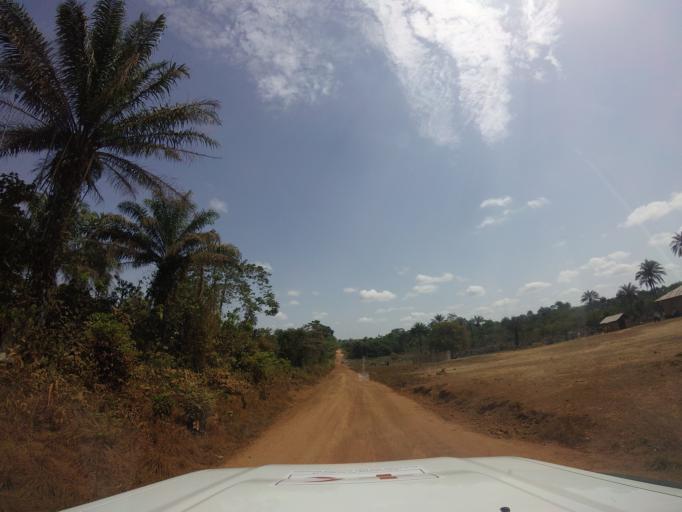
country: LR
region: Grand Cape Mount
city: Robertsport
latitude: 6.9923
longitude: -11.2982
